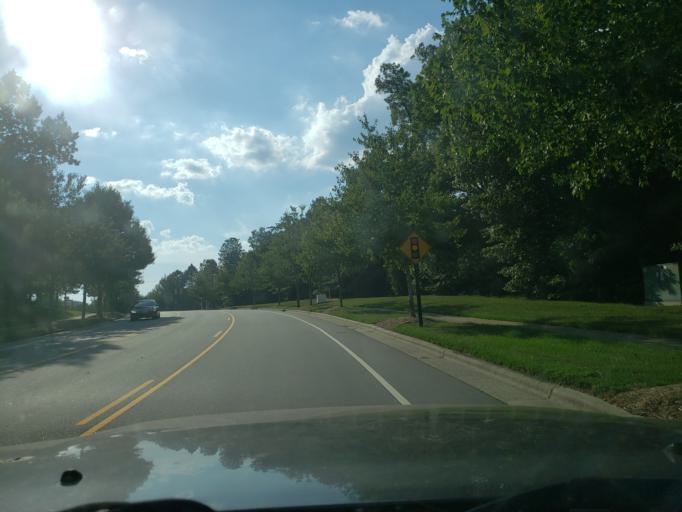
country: US
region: North Carolina
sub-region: Orange County
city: Chapel Hill
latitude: 35.9057
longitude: -79.0077
